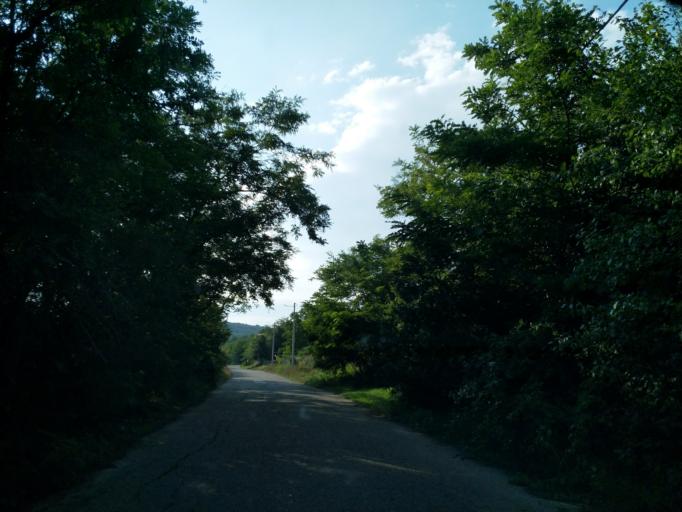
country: RS
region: Central Serbia
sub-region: Pomoravski Okrug
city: Jagodina
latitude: 44.0055
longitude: 21.1808
